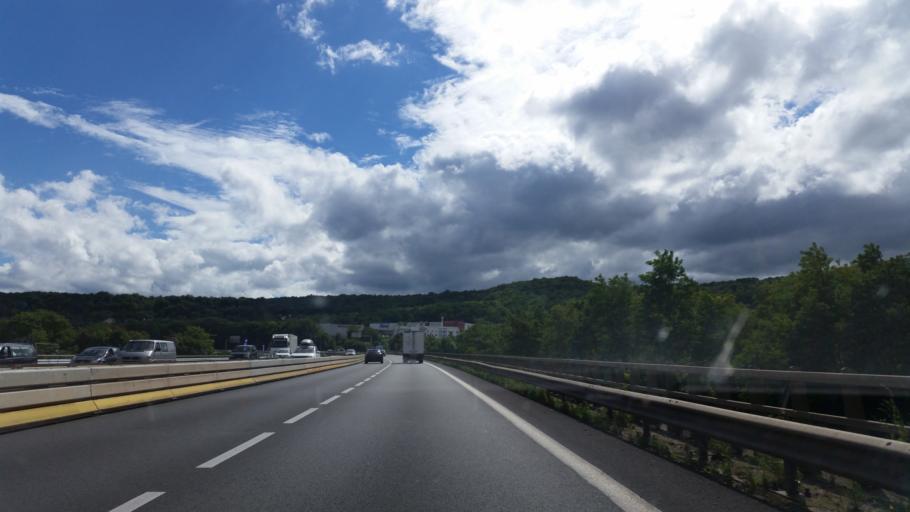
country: FR
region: Lorraine
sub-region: Departement de Meurthe-et-Moselle
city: Bouxieres-aux-Dames
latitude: 48.7467
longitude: 6.1544
